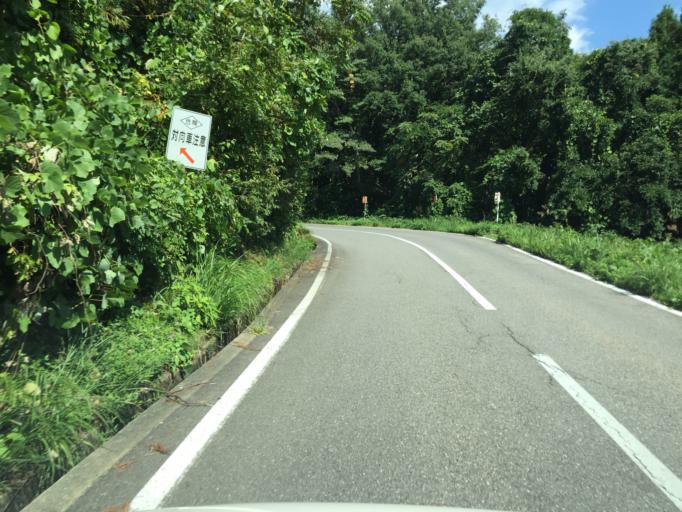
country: JP
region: Fukushima
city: Inawashiro
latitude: 37.5753
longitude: 140.0268
